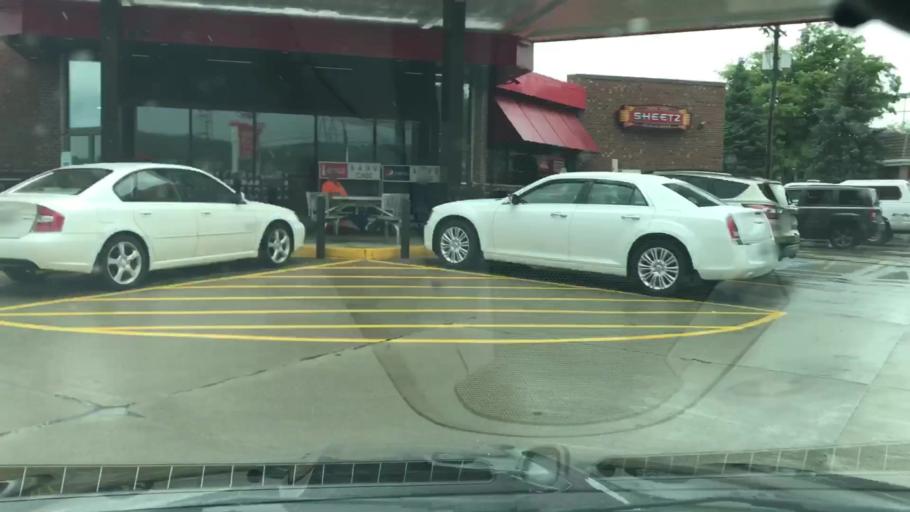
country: US
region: Pennsylvania
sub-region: Westmoreland County
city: New Stanton
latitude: 40.2187
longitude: -79.6098
